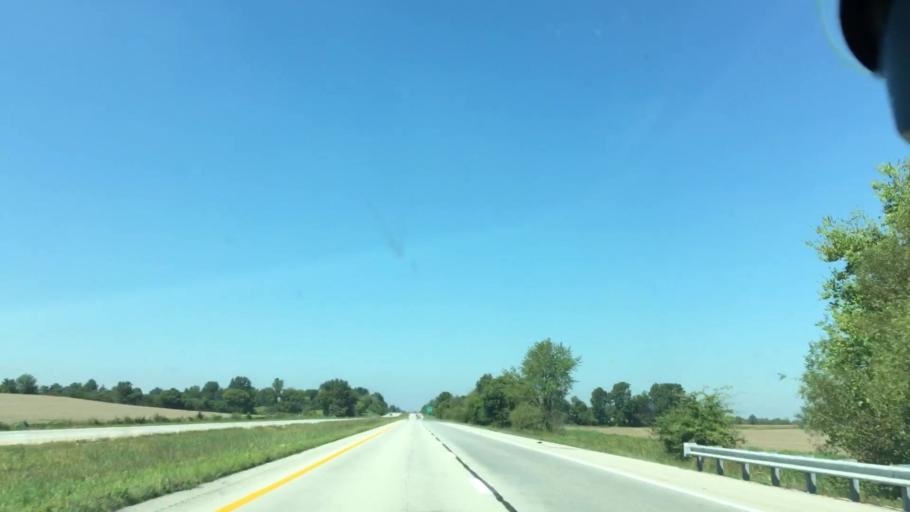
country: US
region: Kentucky
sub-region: Henderson County
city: Henderson
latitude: 37.7667
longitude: -87.5333
